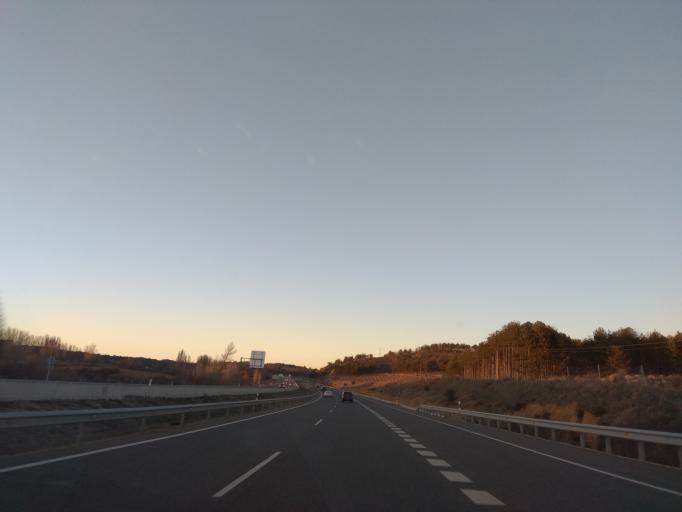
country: ES
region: Castille and Leon
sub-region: Provincia de Burgos
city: Oquillas
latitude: 41.7848
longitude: -3.6972
